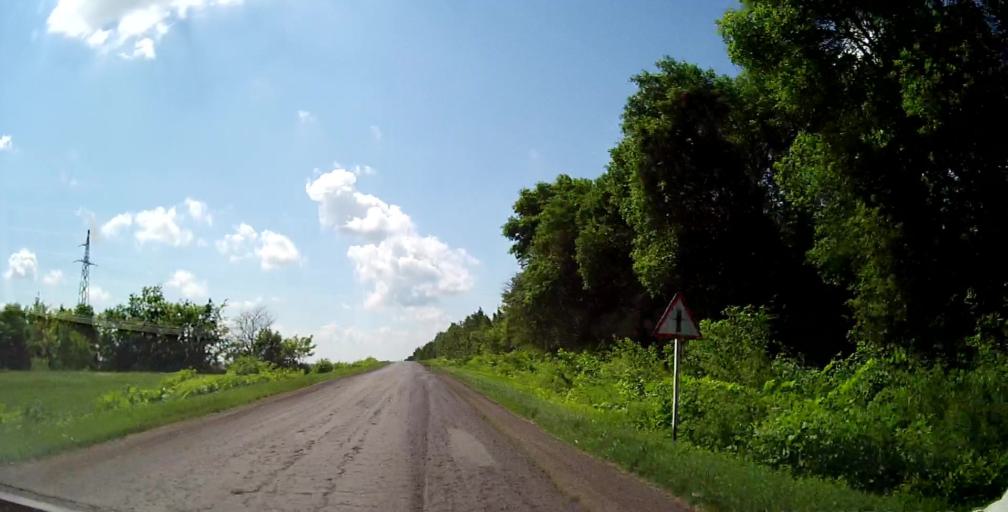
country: RU
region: Lipetsk
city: Chaplygin
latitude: 53.2930
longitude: 39.9566
